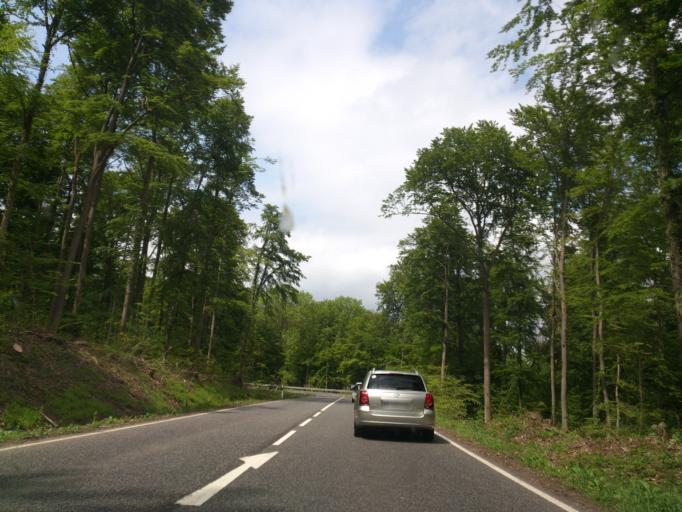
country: DE
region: Hesse
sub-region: Regierungsbezirk Kassel
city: Calden
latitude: 51.3473
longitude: 9.3765
